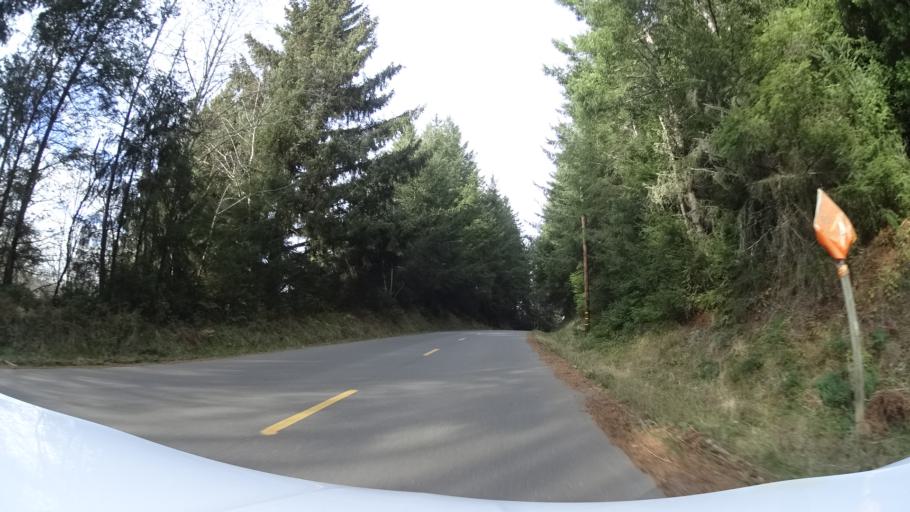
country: US
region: California
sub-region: Humboldt County
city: Ferndale
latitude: 40.5547
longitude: -124.2735
